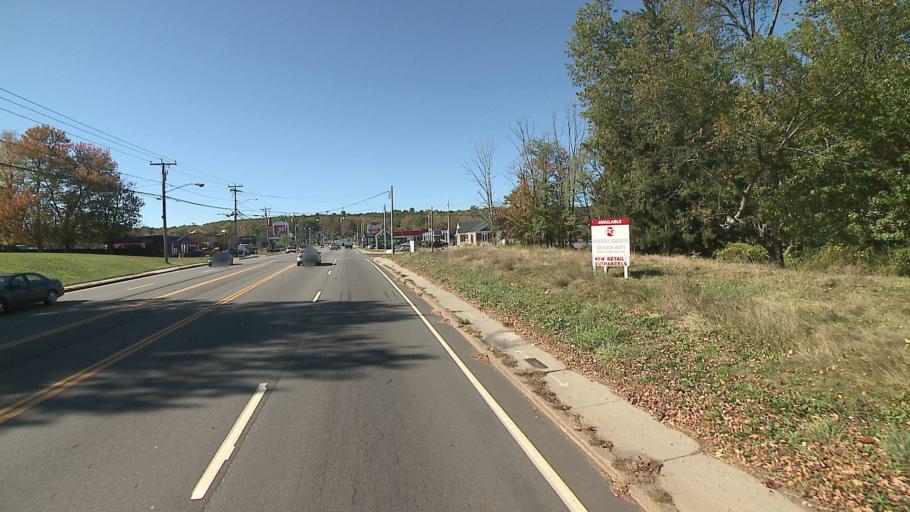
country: US
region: Connecticut
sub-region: Middlesex County
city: Middletown
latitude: 41.5547
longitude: -72.6790
